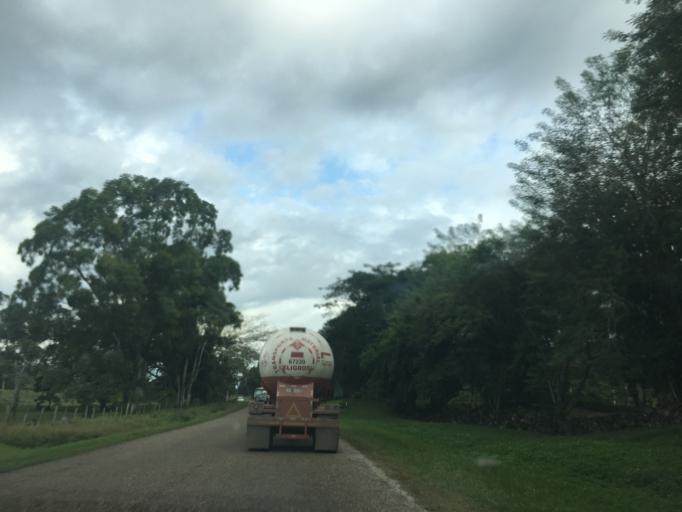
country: BZ
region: Cayo
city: San Ignacio
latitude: 17.2032
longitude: -88.9529
